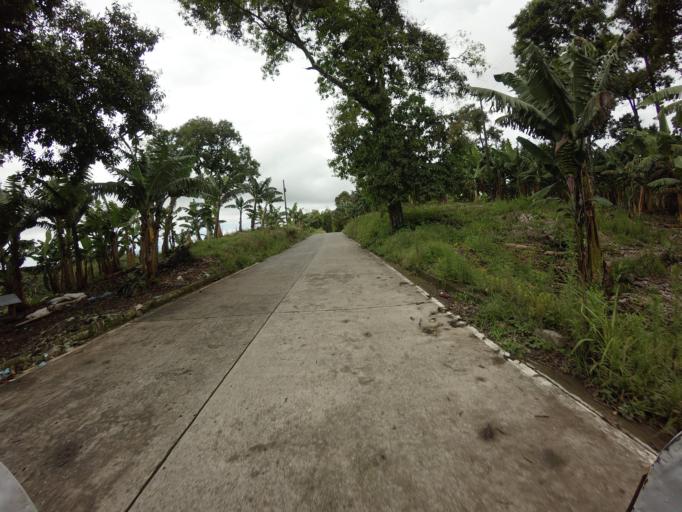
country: CO
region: Valle del Cauca
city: Ulloa
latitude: 4.6999
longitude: -75.7530
